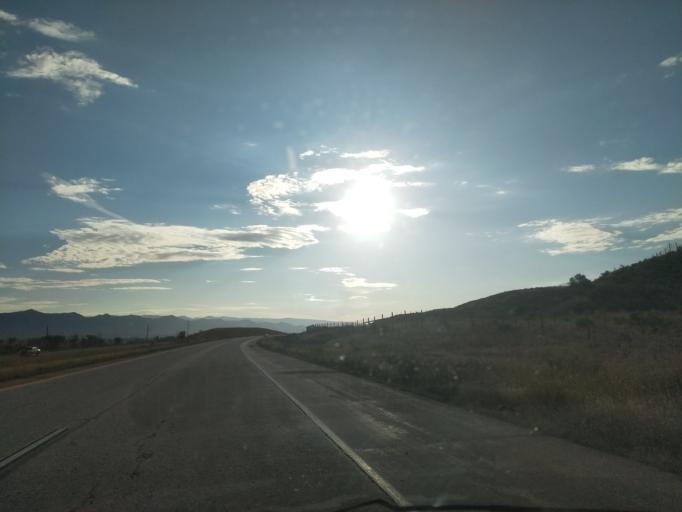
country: US
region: Colorado
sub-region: Garfield County
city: Rifle
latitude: 39.5288
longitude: -107.7422
